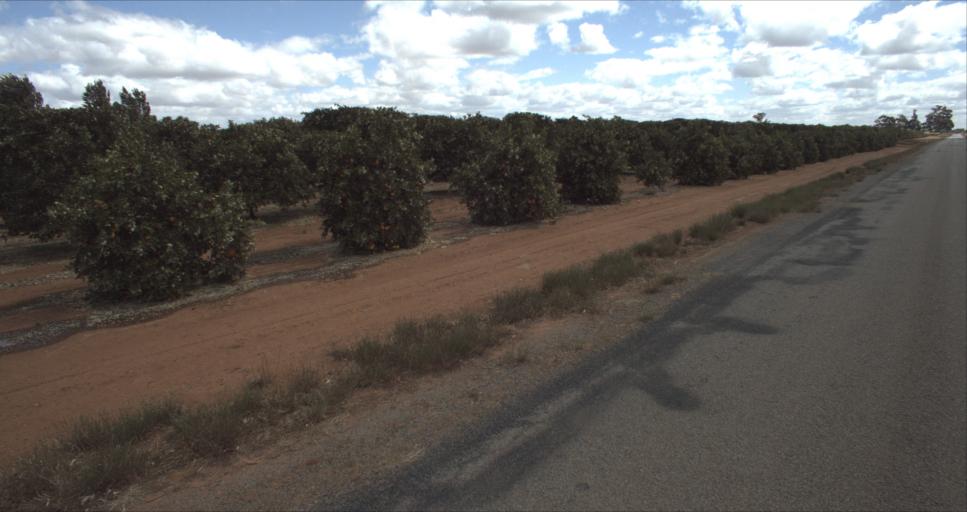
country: AU
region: New South Wales
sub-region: Leeton
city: Leeton
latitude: -34.5809
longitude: 146.4079
